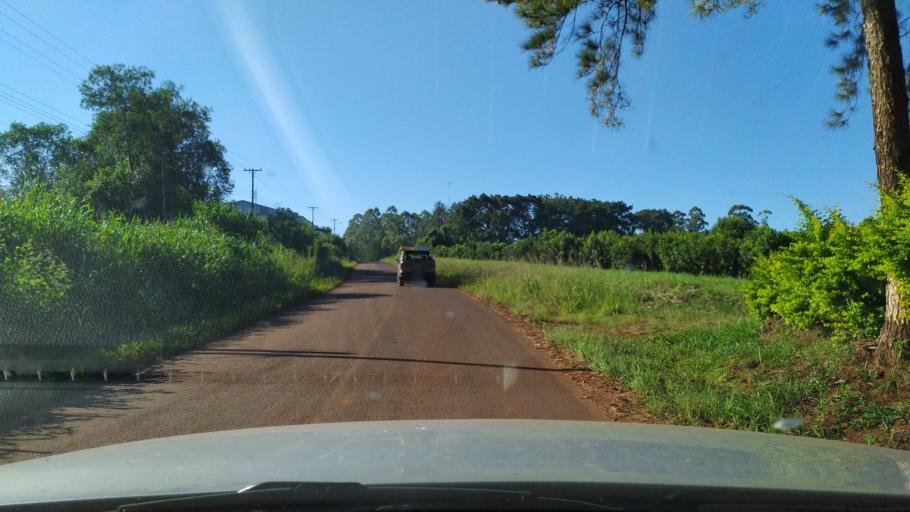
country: AR
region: Misiones
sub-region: Departamento de Montecarlo
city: Montecarlo
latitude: -26.6039
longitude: -54.7020
